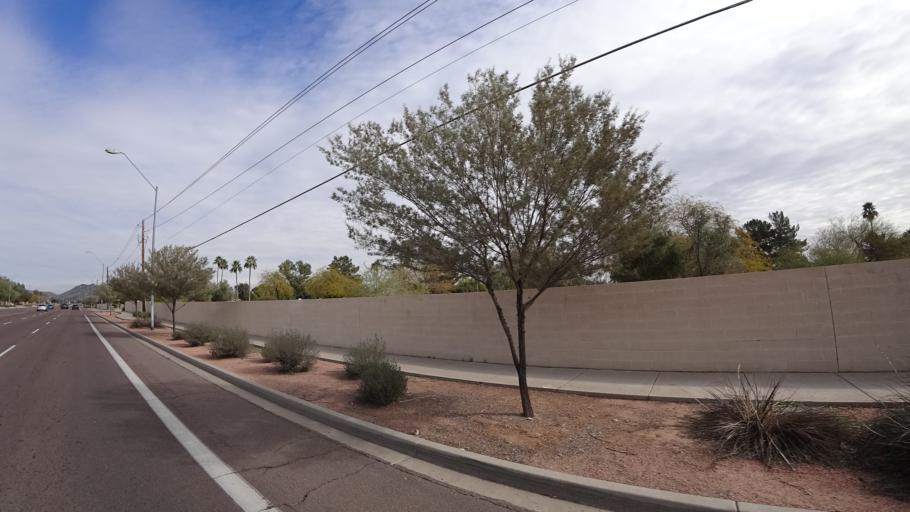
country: US
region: Arizona
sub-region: Maricopa County
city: Peoria
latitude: 33.6420
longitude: -112.1690
